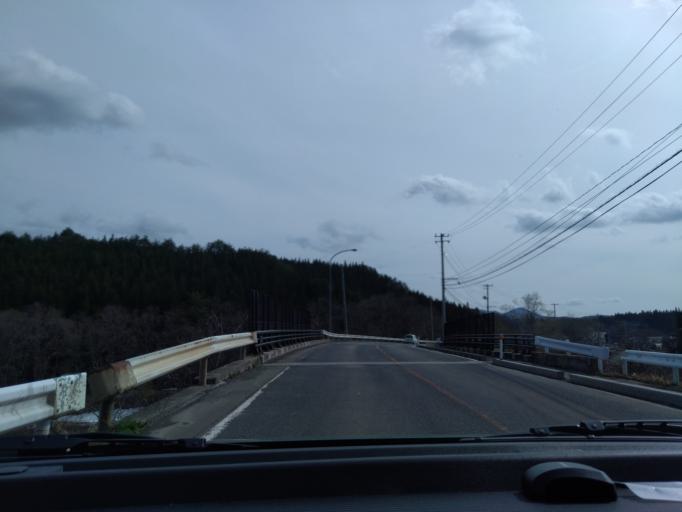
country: JP
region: Akita
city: Yokotemachi
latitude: 39.3022
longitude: 140.7391
